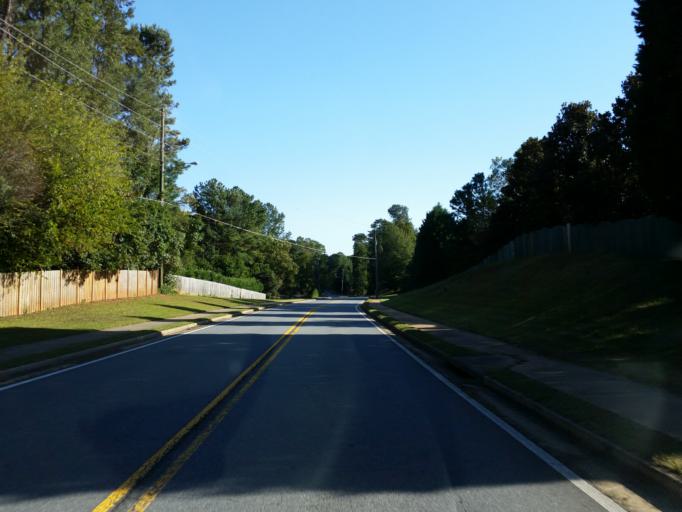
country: US
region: Georgia
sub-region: Cobb County
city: Marietta
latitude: 34.0006
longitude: -84.4724
